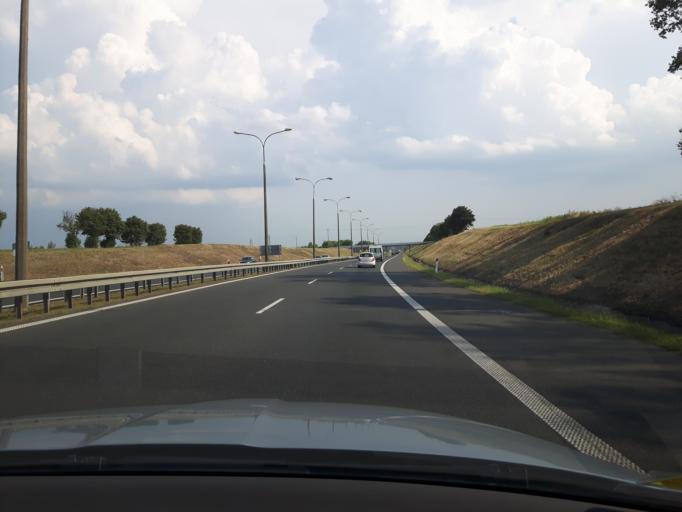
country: PL
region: Masovian Voivodeship
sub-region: Powiat nowodworski
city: Zakroczym
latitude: 52.4377
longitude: 20.6469
